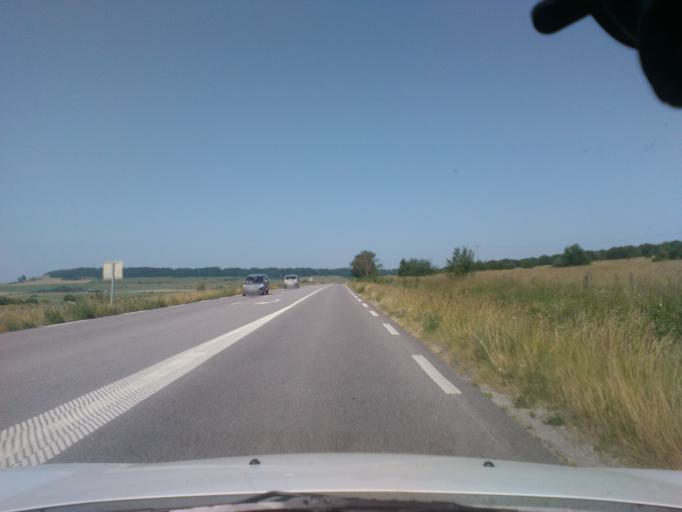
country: FR
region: Lorraine
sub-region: Departement des Vosges
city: Chatenois
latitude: 48.3012
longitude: 5.8139
